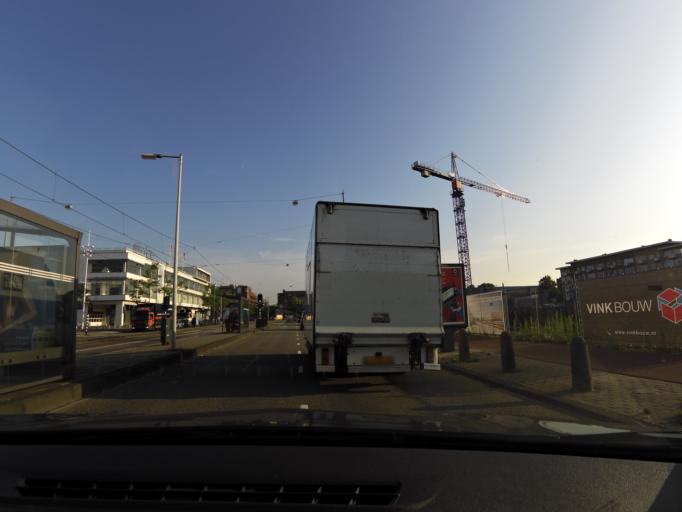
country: NL
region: North Holland
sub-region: Gemeente Amstelveen
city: Amstelveen
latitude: 52.3436
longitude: 4.8572
